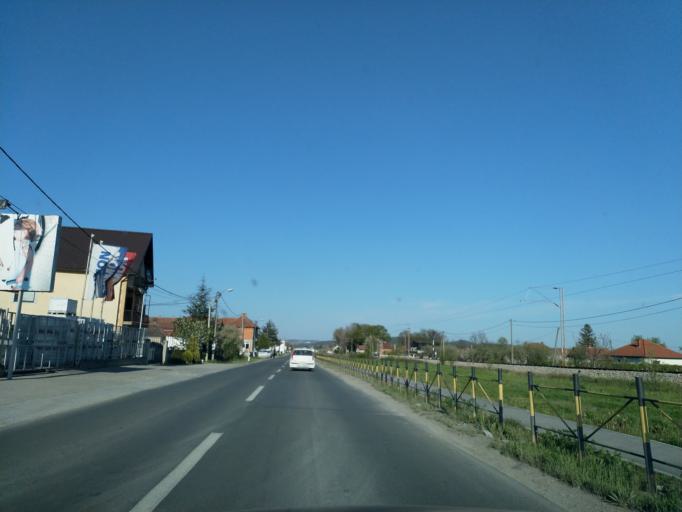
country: RS
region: Central Serbia
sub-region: Kolubarski Okrug
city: Lajkovac
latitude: 44.3648
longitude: 20.1436
